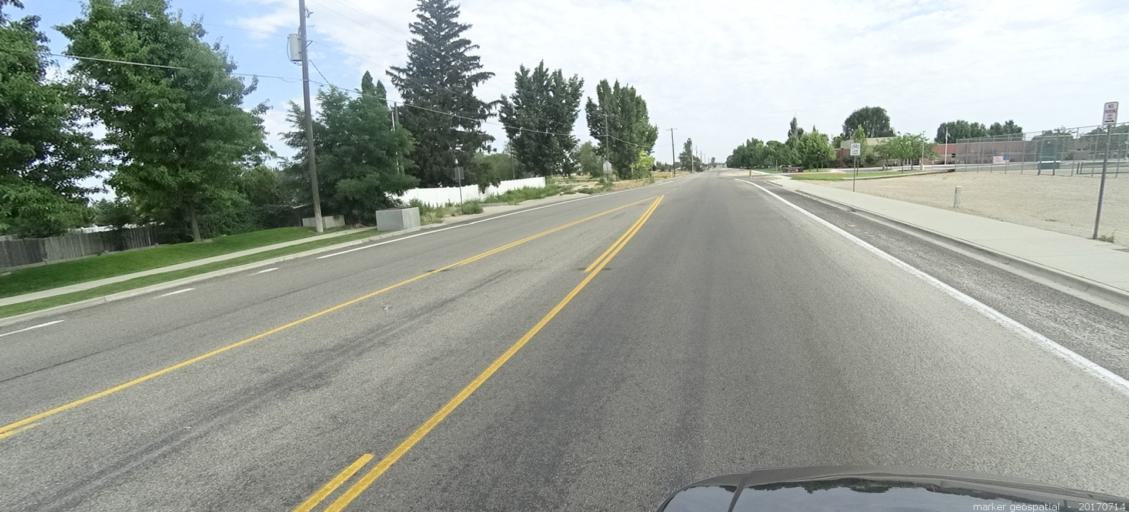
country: US
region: Idaho
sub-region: Ada County
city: Kuna
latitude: 43.4971
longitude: -116.4335
